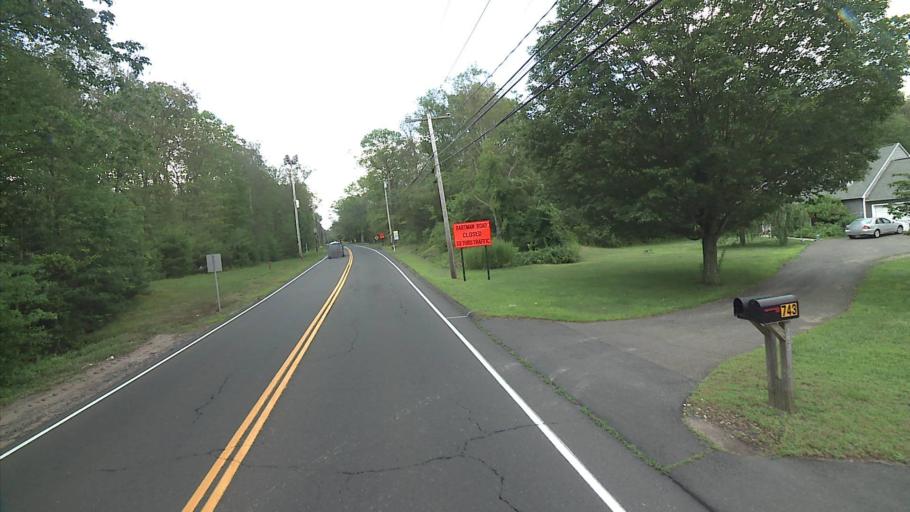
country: US
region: Connecticut
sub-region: Middlesex County
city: Higganum
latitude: 41.4466
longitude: -72.5553
